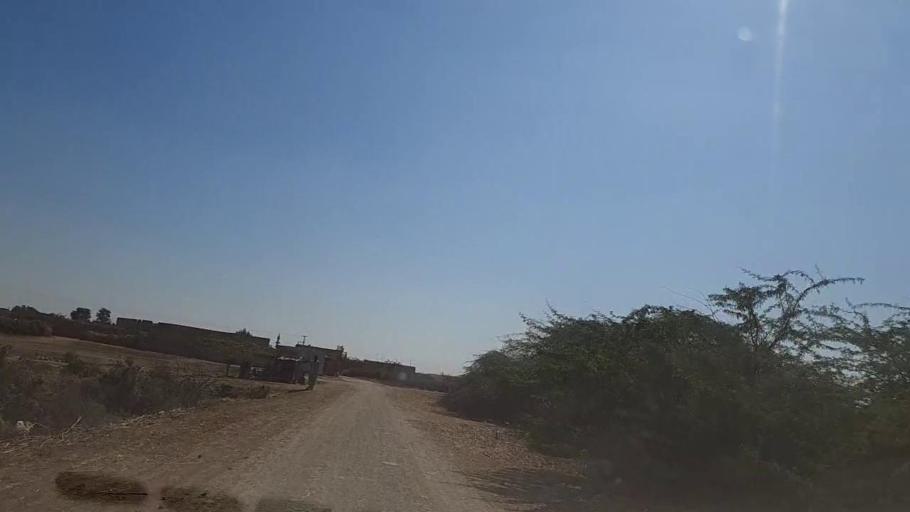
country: PK
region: Sindh
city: Digri
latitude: 25.1008
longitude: 69.1280
